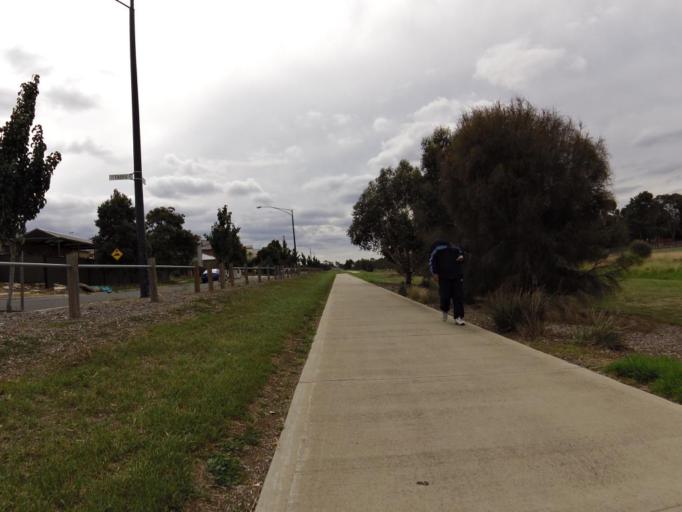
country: AU
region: Victoria
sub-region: Brimbank
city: Cairnlea
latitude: -37.7538
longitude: 144.7957
